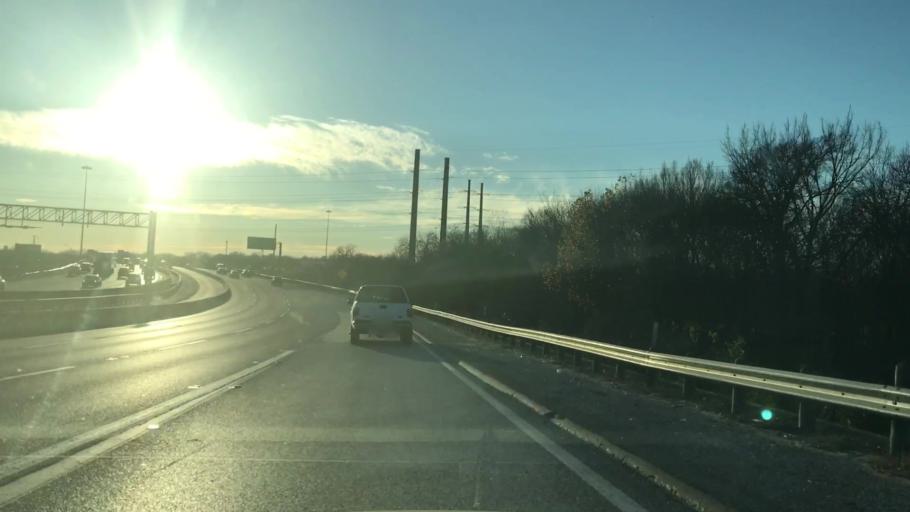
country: US
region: Texas
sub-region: Dallas County
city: Highland Park
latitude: 32.7946
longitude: -96.7247
